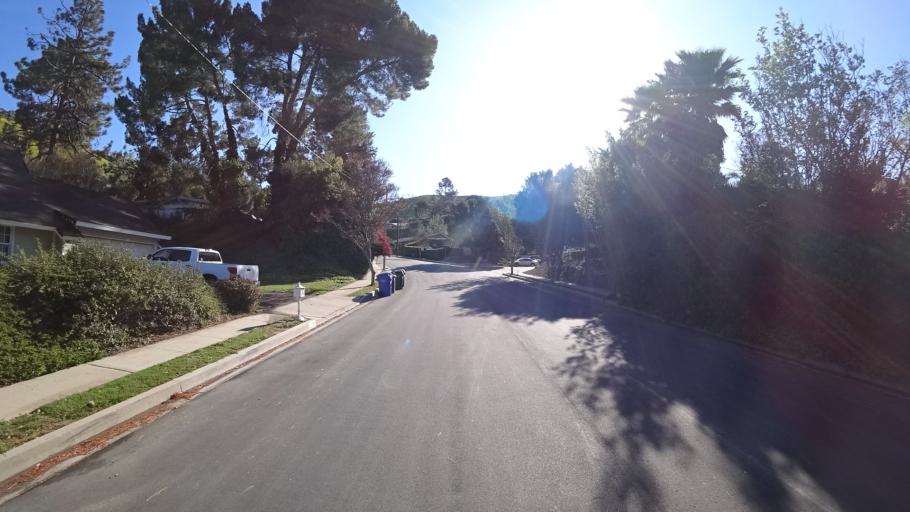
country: US
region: California
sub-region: Ventura County
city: Thousand Oaks
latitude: 34.1901
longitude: -118.8362
